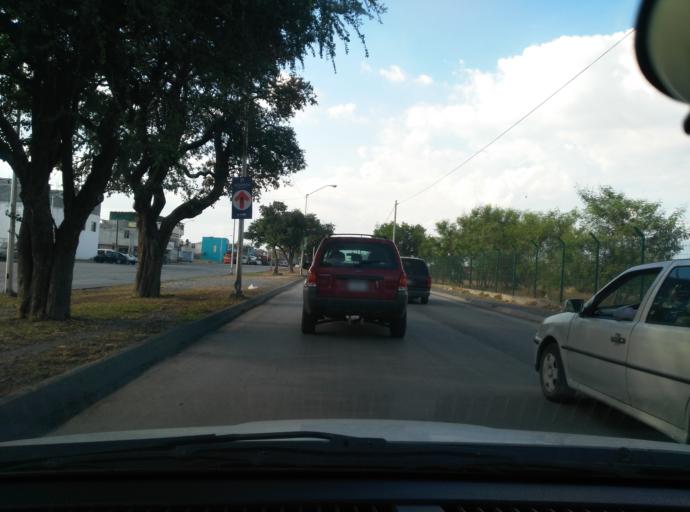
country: MX
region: Nuevo Leon
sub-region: Apodaca
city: Fraccionamiento Cosmopolis Octavo Sector
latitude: 25.7652
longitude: -100.2424
